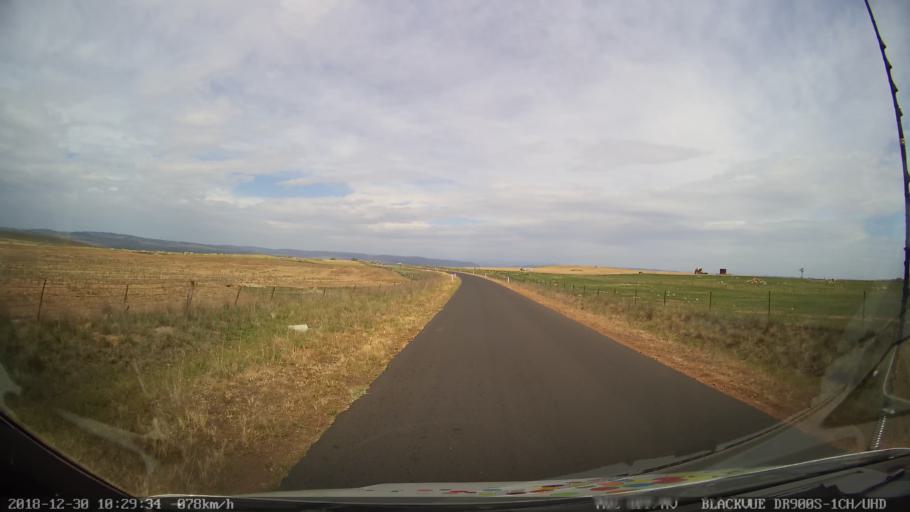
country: AU
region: New South Wales
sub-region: Snowy River
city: Berridale
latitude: -36.5012
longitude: 148.9071
